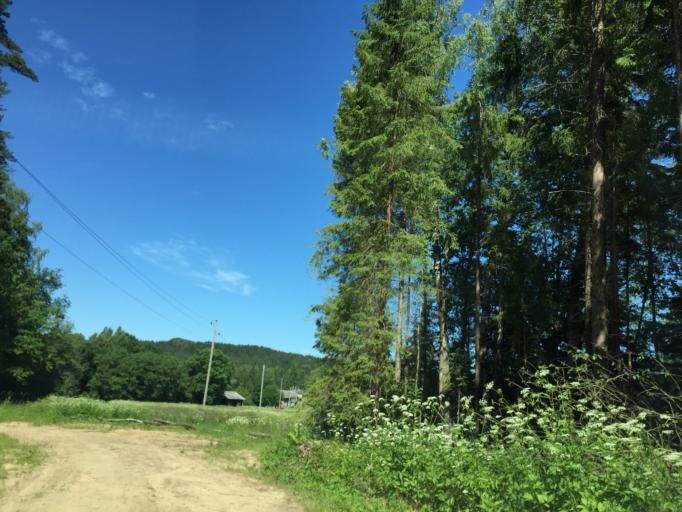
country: LV
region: Sigulda
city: Sigulda
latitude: 57.2266
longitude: 24.9160
